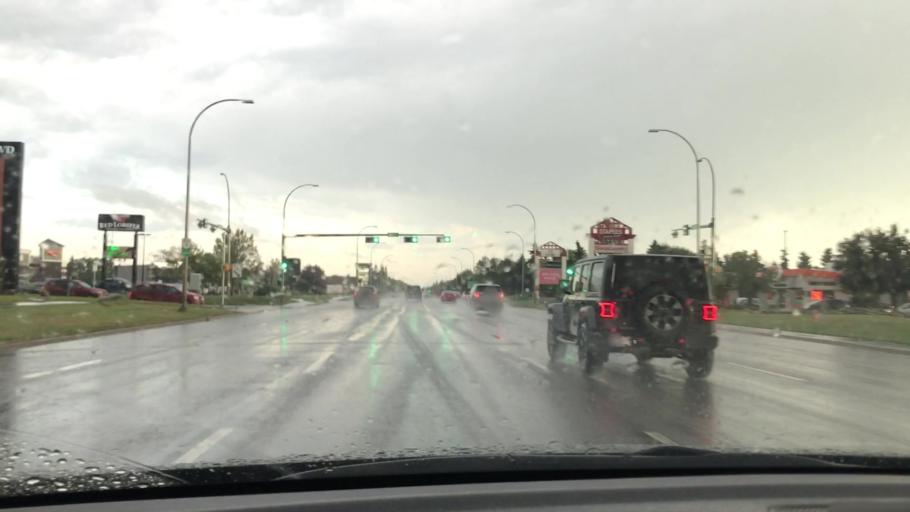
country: CA
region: Alberta
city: Edmonton
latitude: 53.4786
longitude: -113.4956
